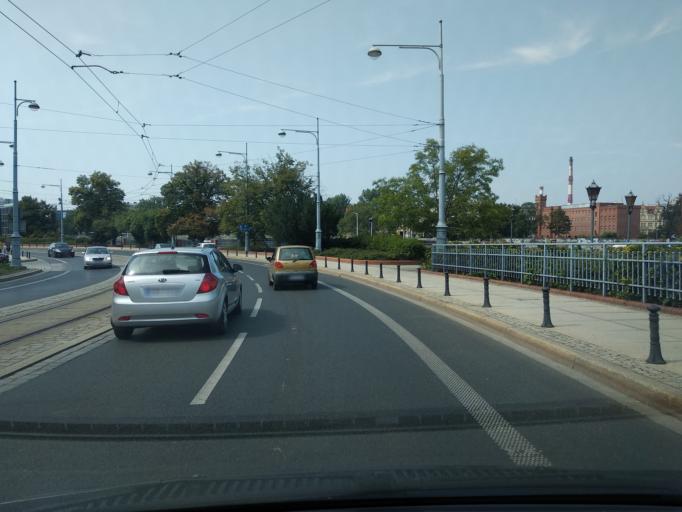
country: PL
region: Lower Silesian Voivodeship
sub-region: Powiat wroclawski
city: Wroclaw
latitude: 51.1146
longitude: 17.0363
